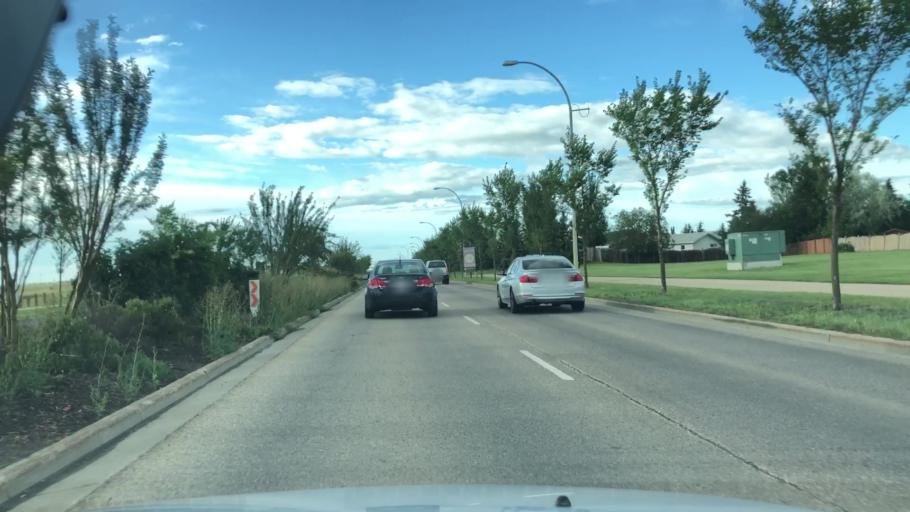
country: CA
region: Alberta
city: St. Albert
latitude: 53.6250
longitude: -113.5411
